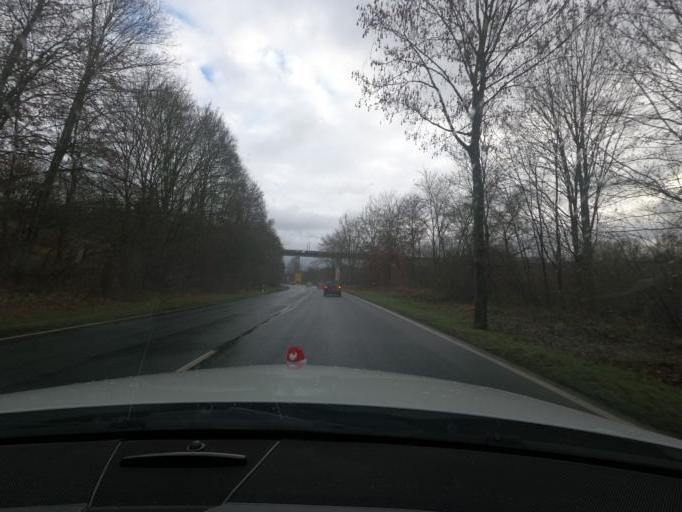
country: DE
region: Lower Saxony
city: Kreiensen
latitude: 51.8696
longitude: 9.9848
